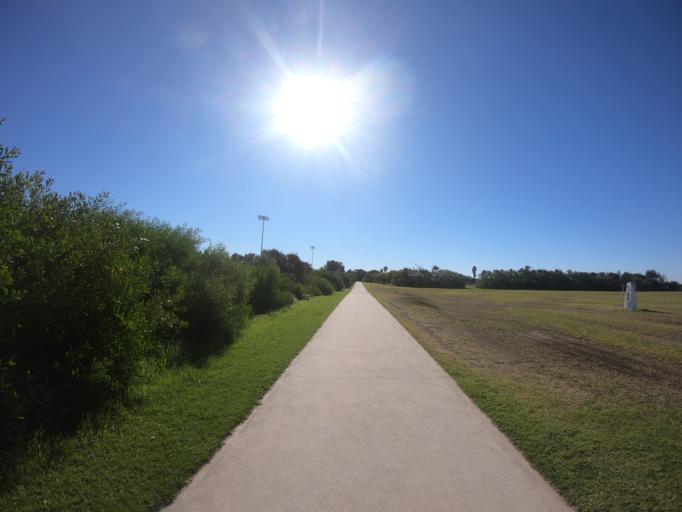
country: AU
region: New South Wales
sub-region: Wollongong
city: Fairy Meadow
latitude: -34.3936
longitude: 150.9053
